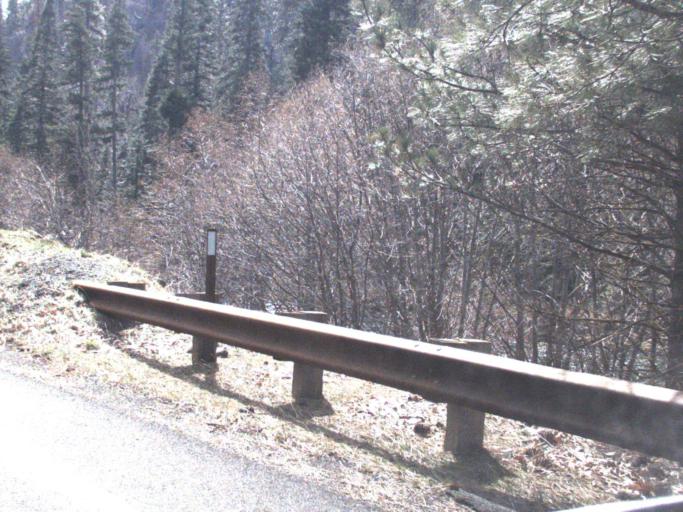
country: US
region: Washington
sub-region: Kittitas County
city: Cle Elum
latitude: 46.9706
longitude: -121.0948
